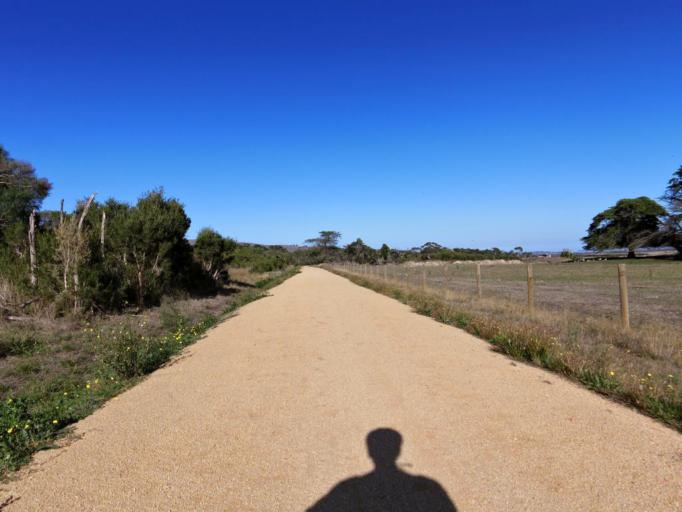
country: AU
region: Victoria
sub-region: Bass Coast
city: North Wonthaggi
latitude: -38.4982
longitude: 145.5066
